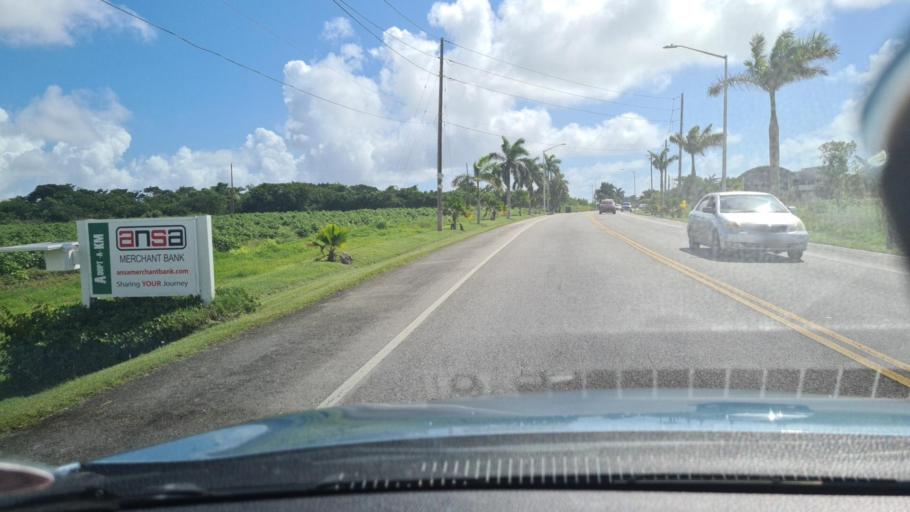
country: BB
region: Christ Church
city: Oistins
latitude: 13.0824
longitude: -59.5337
